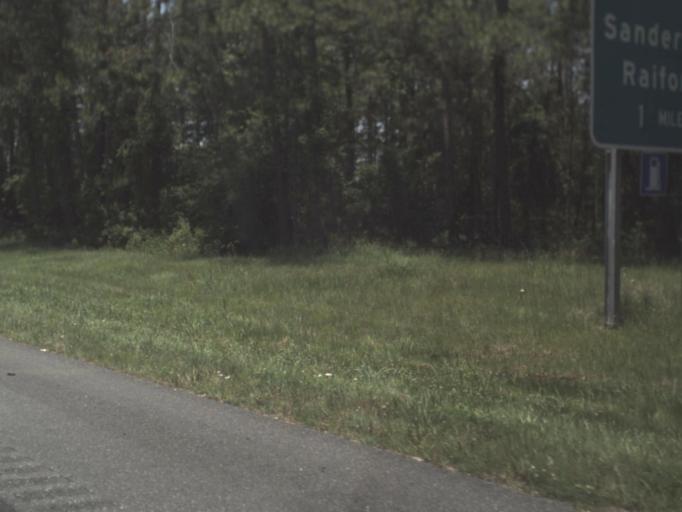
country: US
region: Florida
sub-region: Baker County
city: Macclenny
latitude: 30.2436
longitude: -82.2450
